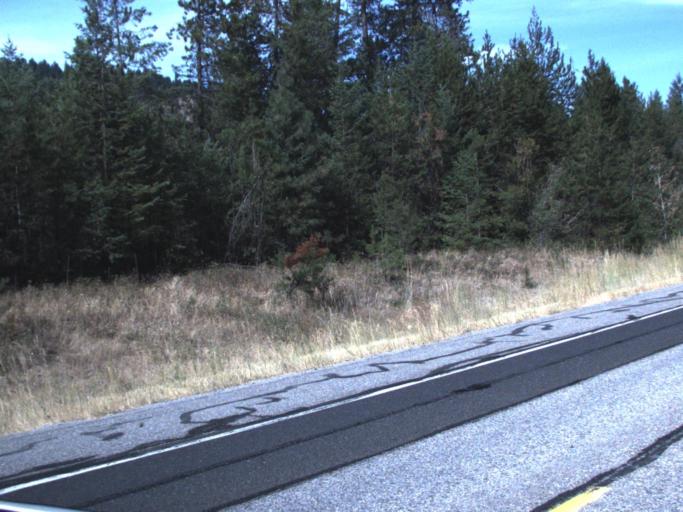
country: US
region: Washington
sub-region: Stevens County
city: Chewelah
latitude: 48.1139
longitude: -117.6459
